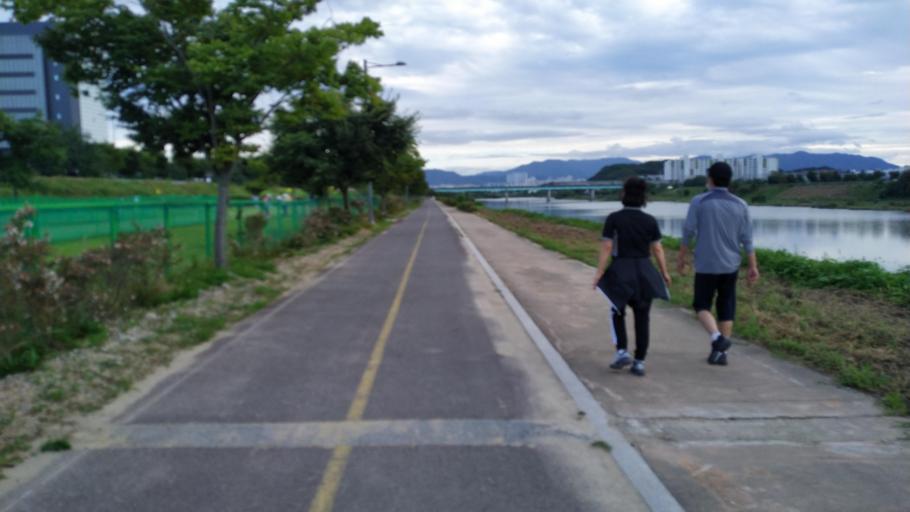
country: KR
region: Daegu
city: Daegu
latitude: 35.9247
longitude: 128.6325
